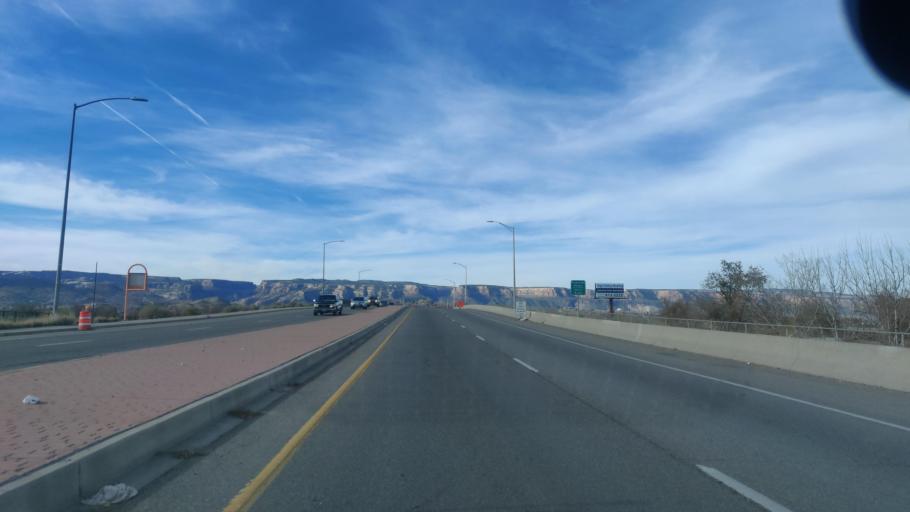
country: US
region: Colorado
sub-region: Mesa County
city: Grand Junction
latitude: 39.0708
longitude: -108.5736
